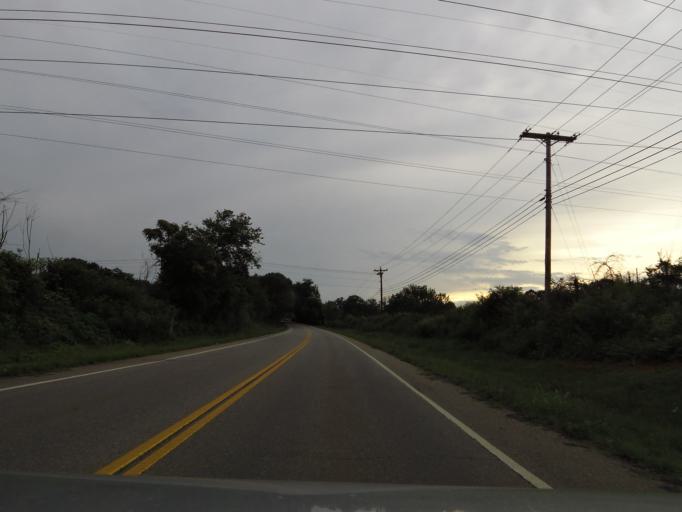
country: US
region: Tennessee
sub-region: Blount County
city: Alcoa
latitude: 35.8063
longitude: -83.9672
